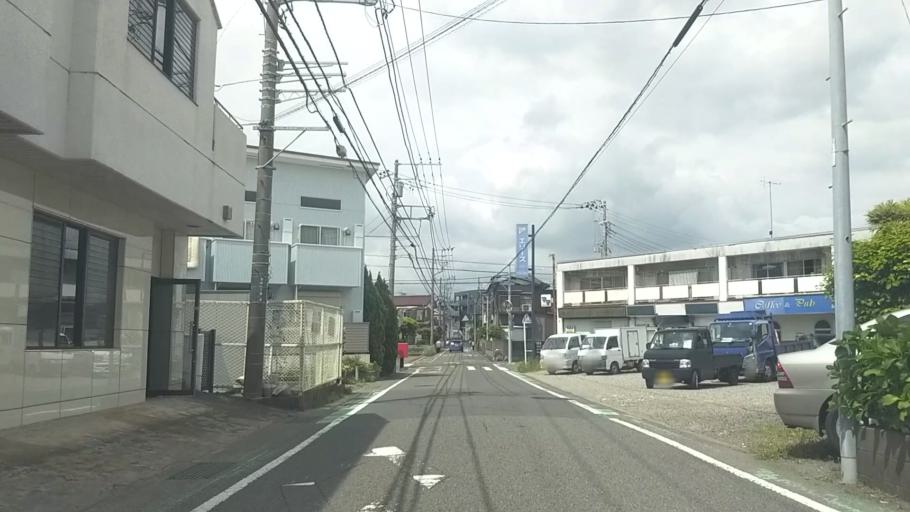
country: JP
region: Kanagawa
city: Fujisawa
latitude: 35.3447
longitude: 139.4554
